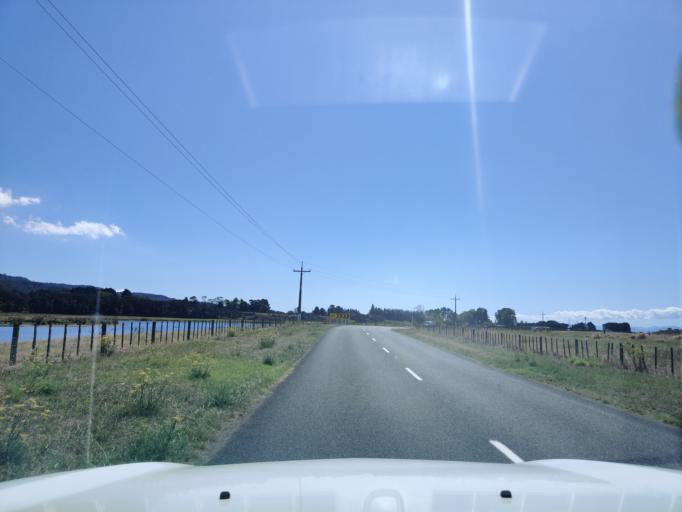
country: NZ
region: Waikato
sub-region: Thames-Coromandel District
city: Thames
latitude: -37.0609
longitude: 175.2982
